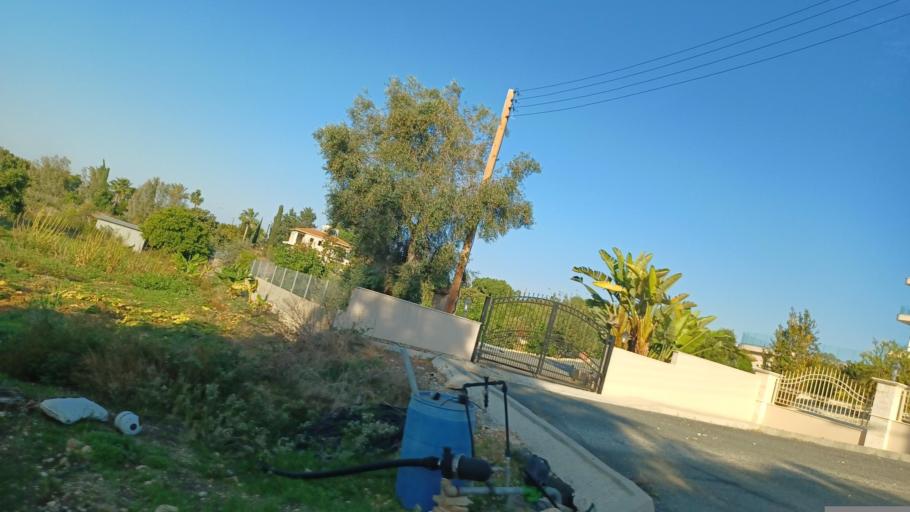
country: CY
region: Pafos
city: Pegeia
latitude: 34.8797
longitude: 32.3445
